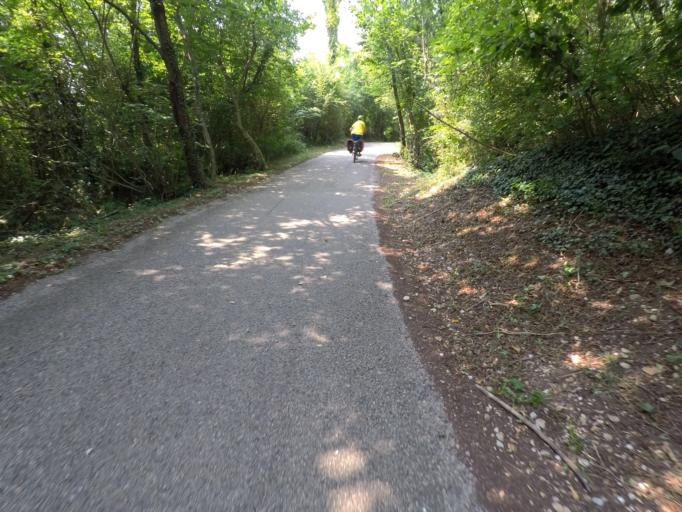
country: IT
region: Friuli Venezia Giulia
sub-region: Provincia di Pordenone
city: Montereale Valcellina
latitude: 46.1373
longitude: 12.6465
